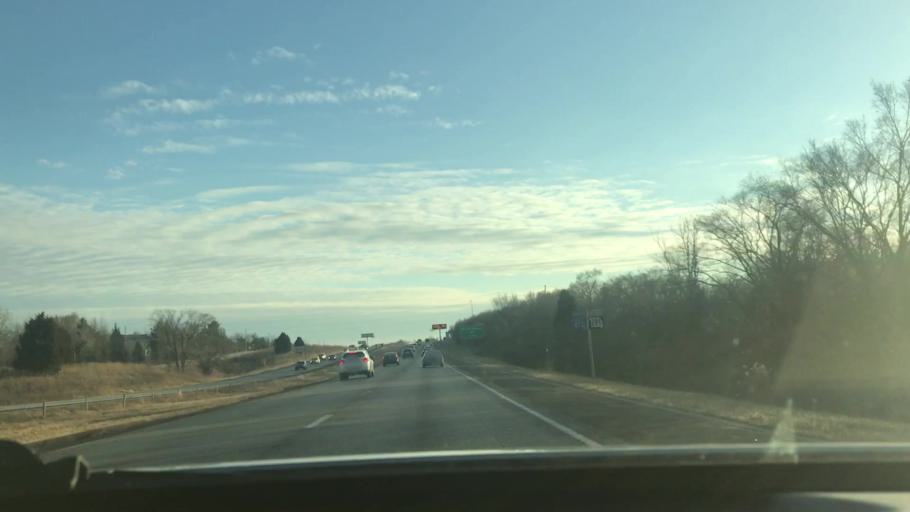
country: US
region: Missouri
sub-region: Jackson County
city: Blue Springs
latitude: 38.9989
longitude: -94.3574
